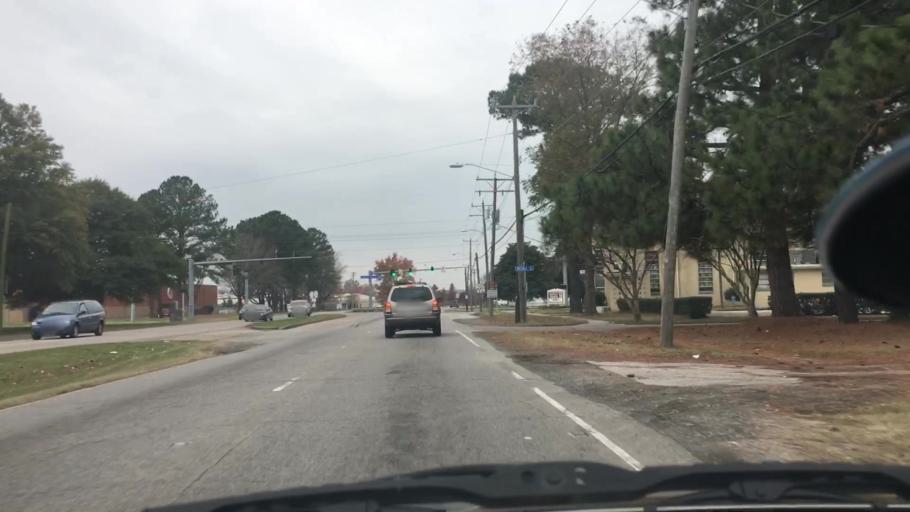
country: US
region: Virginia
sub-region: City of Norfolk
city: Norfolk
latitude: 36.8685
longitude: -76.2286
